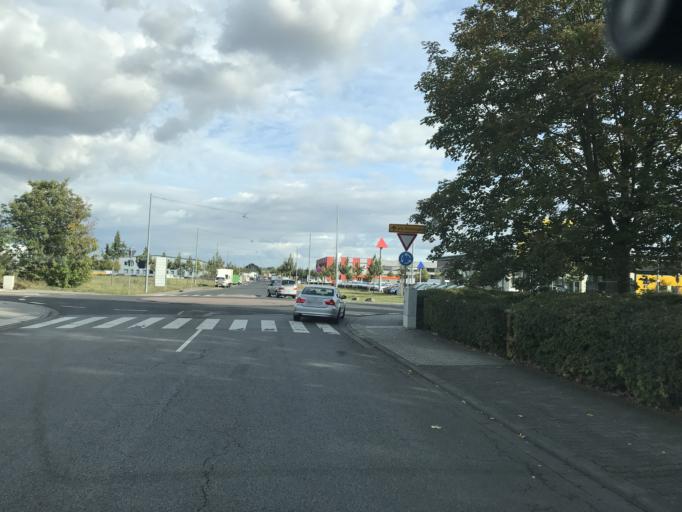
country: DE
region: Rheinland-Pfalz
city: Mainz
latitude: 50.0289
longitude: 8.2812
